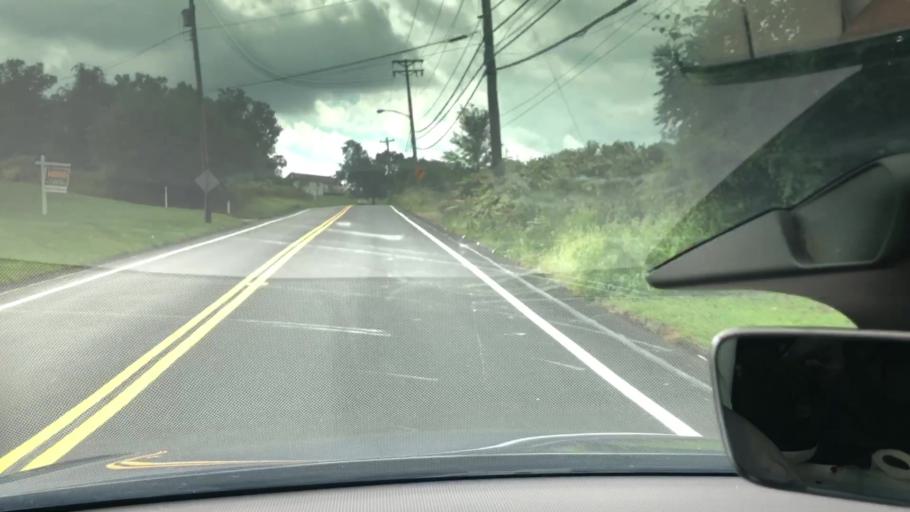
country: US
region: Pennsylvania
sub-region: Allegheny County
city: Wilmerding
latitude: 40.3927
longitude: -79.8192
